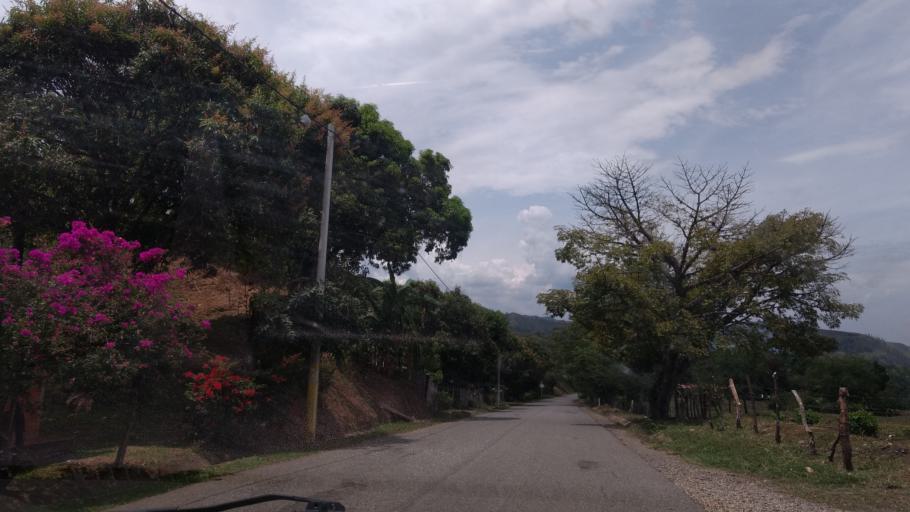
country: CO
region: Cauca
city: Buenos Aires
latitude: 3.0583
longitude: -76.6587
